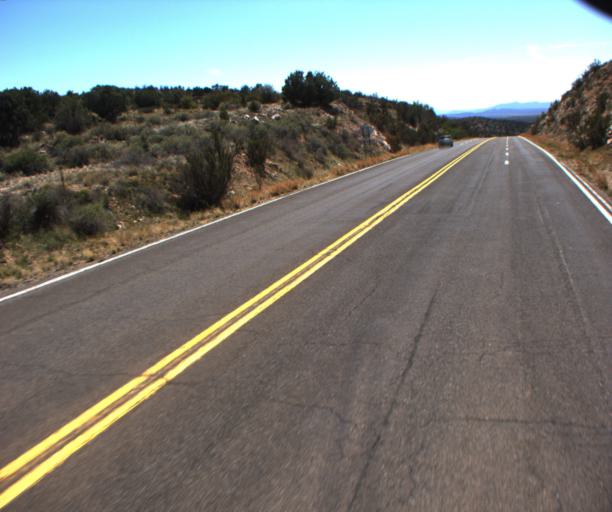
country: US
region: Arizona
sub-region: Mohave County
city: Peach Springs
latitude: 35.5482
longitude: -113.3961
